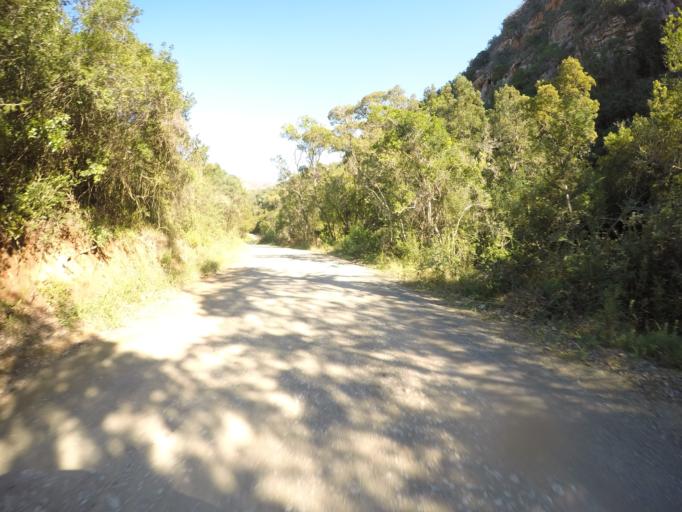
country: ZA
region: Eastern Cape
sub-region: Cacadu District Municipality
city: Kareedouw
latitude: -33.6536
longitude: 24.5195
